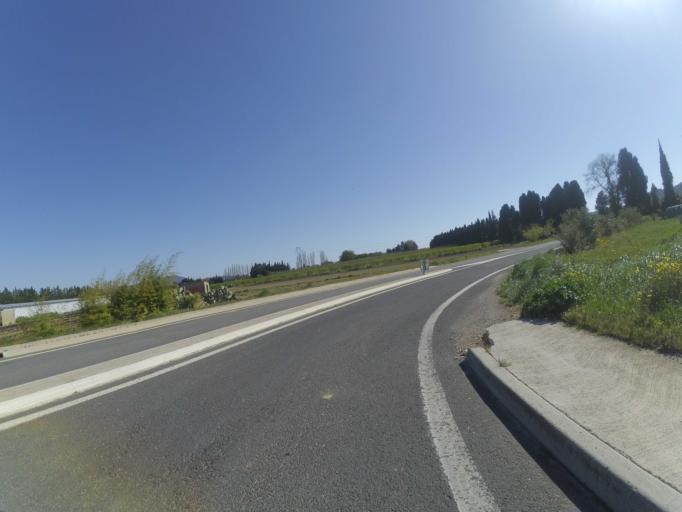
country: FR
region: Languedoc-Roussillon
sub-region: Departement des Pyrenees-Orientales
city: Ille-sur-Tet
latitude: 42.6641
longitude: 2.6336
